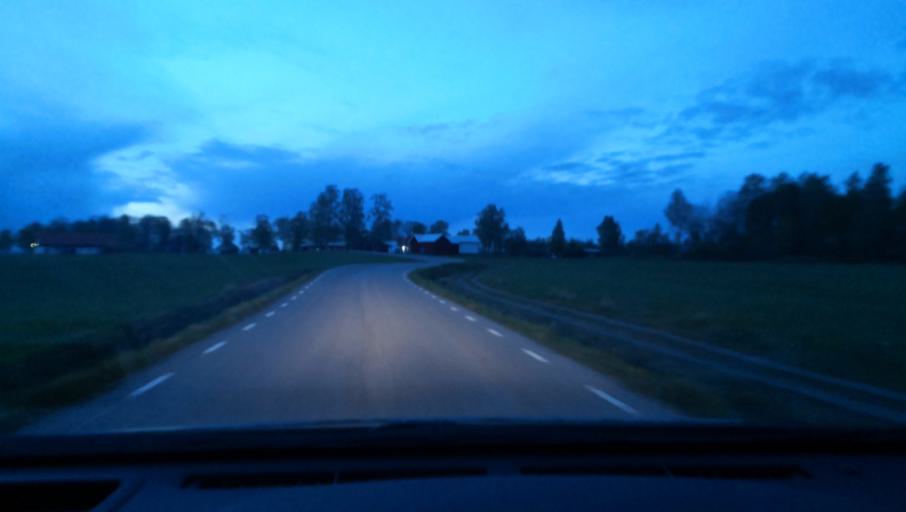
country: SE
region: OErebro
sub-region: Orebro Kommun
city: Vintrosa
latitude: 59.1315
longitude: 14.9984
